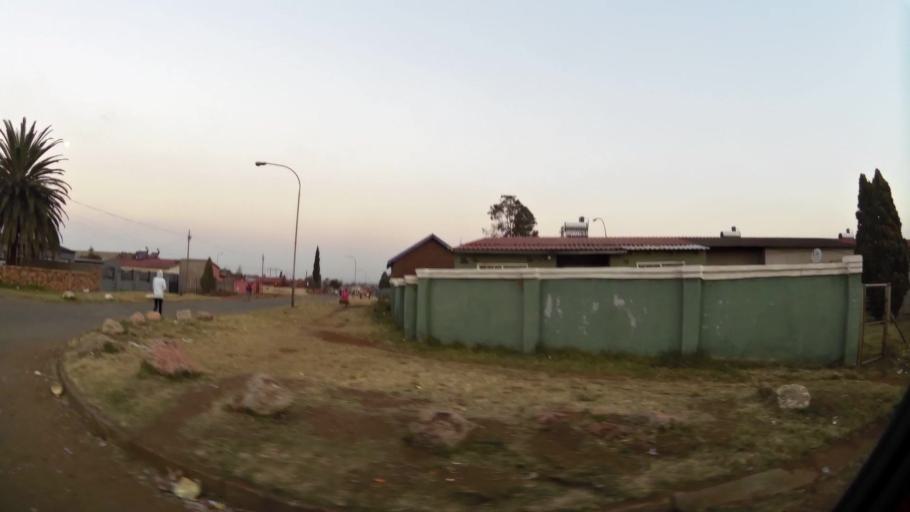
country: ZA
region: Gauteng
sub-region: City of Johannesburg Metropolitan Municipality
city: Soweto
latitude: -26.2940
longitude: 27.8709
